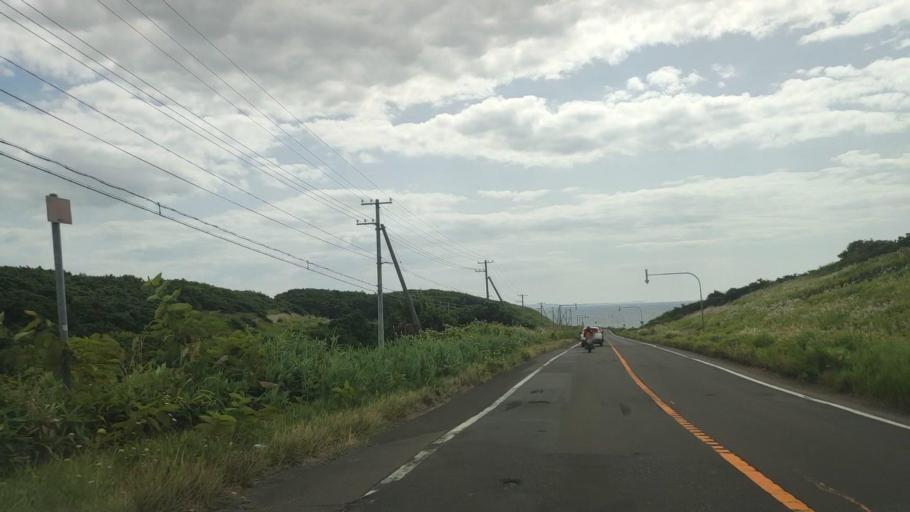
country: JP
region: Hokkaido
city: Rumoi
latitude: 44.5121
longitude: 141.7662
